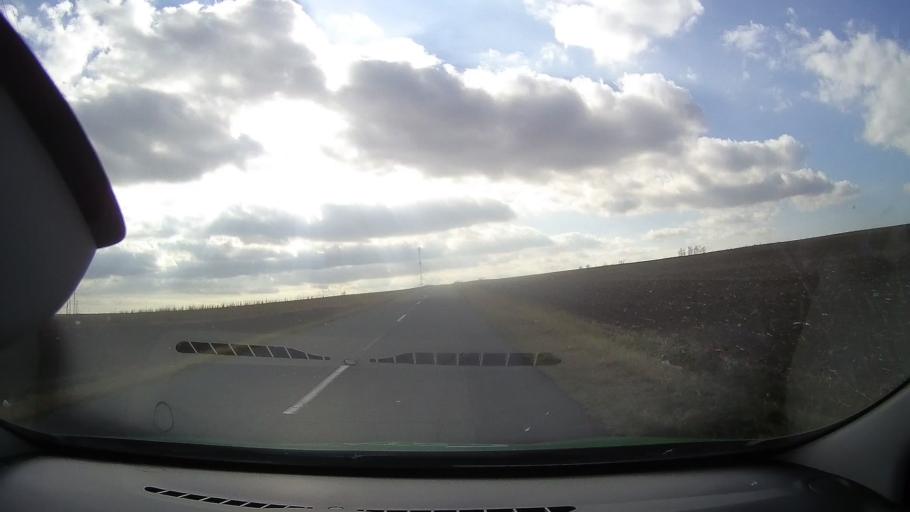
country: RO
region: Constanta
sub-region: Comuna Sacele
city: Sacele
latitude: 44.4948
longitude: 28.6564
